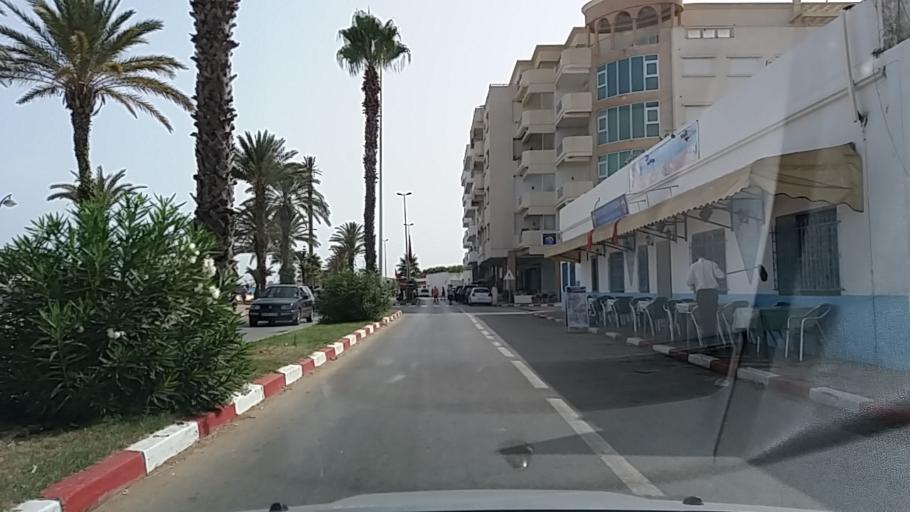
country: MA
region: Tanger-Tetouan
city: Asilah
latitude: 35.4707
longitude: -6.0311
